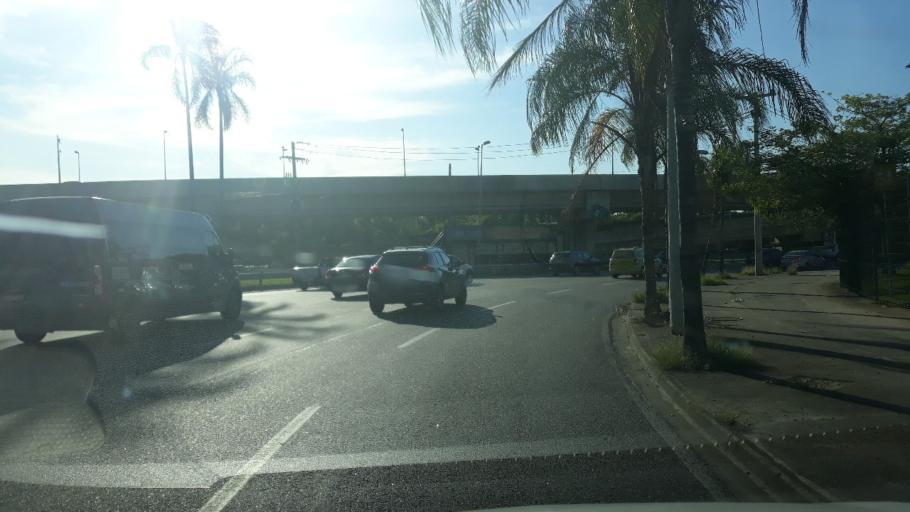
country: BR
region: Rio de Janeiro
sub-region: Sao Joao De Meriti
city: Sao Joao de Meriti
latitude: -22.9737
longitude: -43.3645
